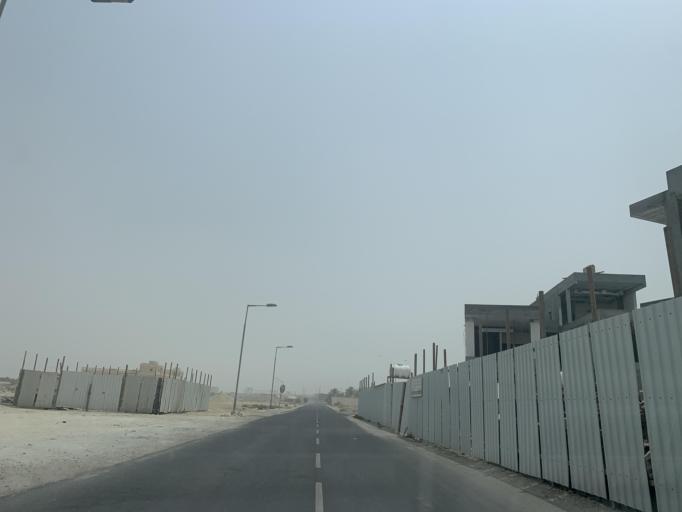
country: BH
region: Central Governorate
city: Madinat Hamad
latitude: 26.1699
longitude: 50.4816
